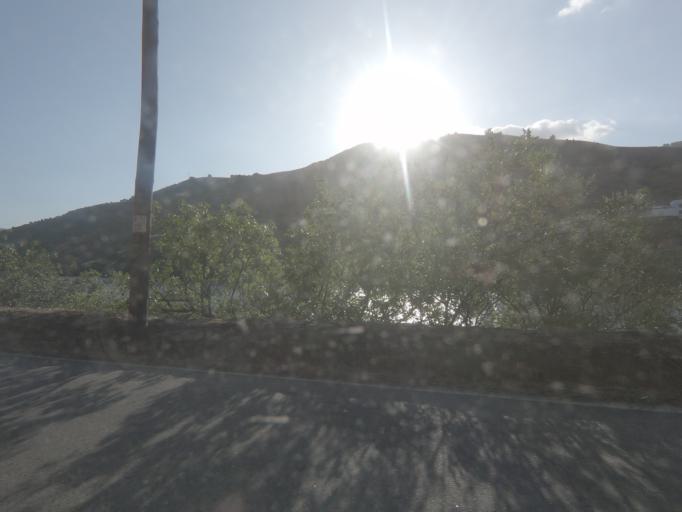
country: PT
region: Viseu
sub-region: Tabuaco
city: Tabuaco
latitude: 41.1813
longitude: -7.5500
